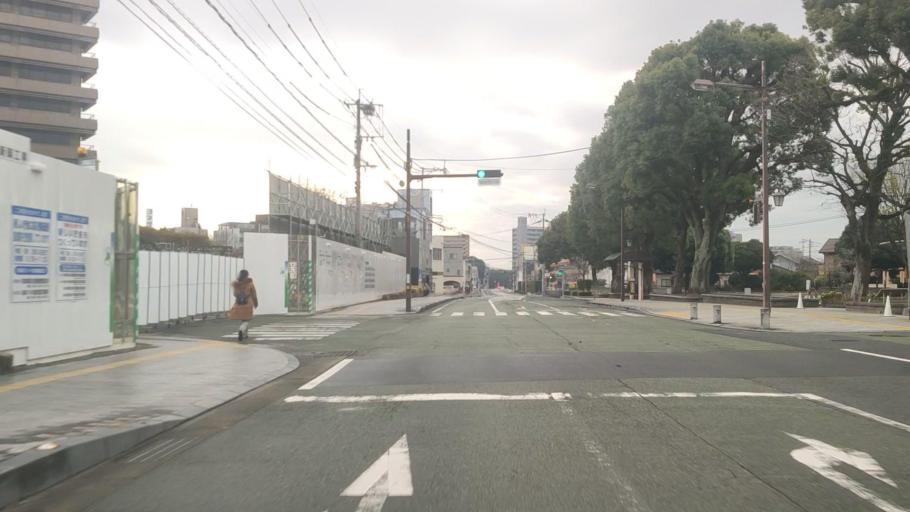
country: JP
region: Kumamoto
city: Kumamoto
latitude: 32.7916
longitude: 130.7405
